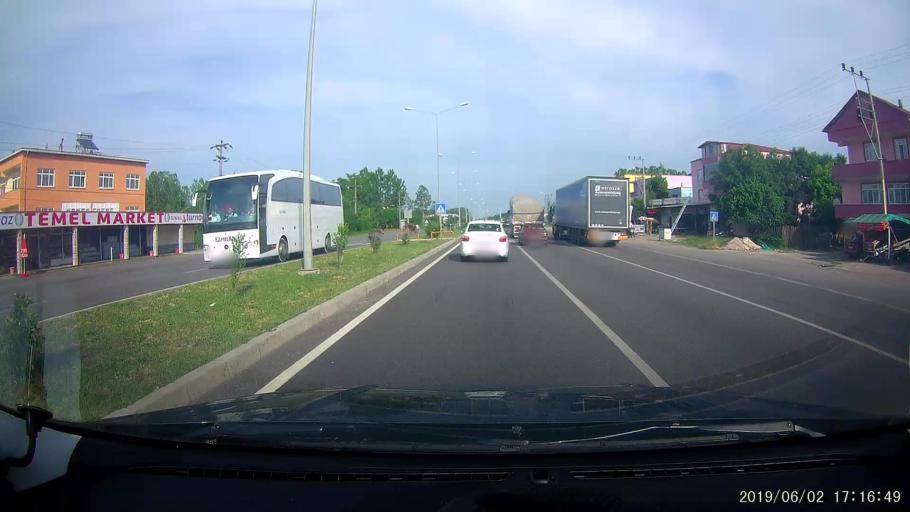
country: TR
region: Samsun
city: Dikbiyik
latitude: 41.2327
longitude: 36.5720
